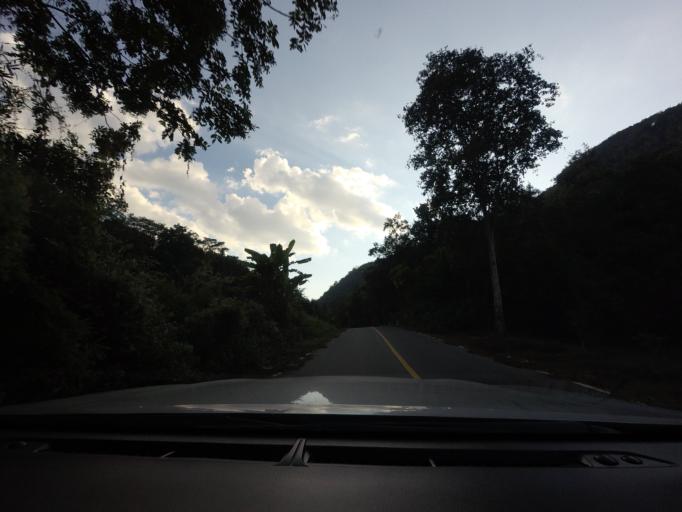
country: TH
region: Chiang Mai
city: Phrao
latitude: 19.5425
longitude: 99.1604
